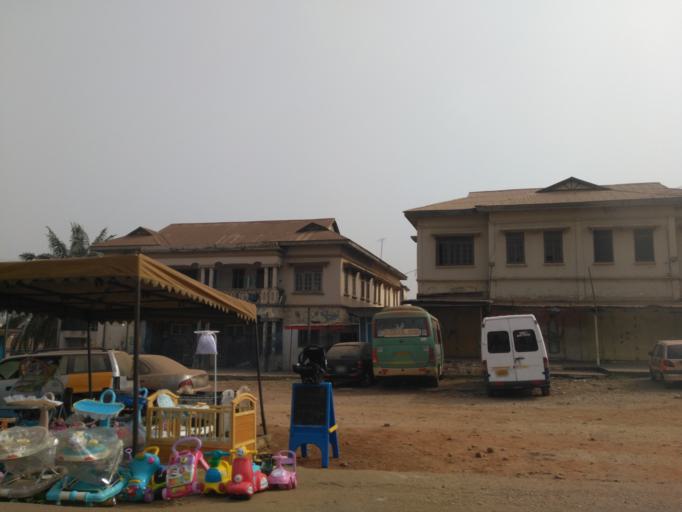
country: GH
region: Ashanti
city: Kumasi
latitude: 6.7075
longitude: -1.6242
